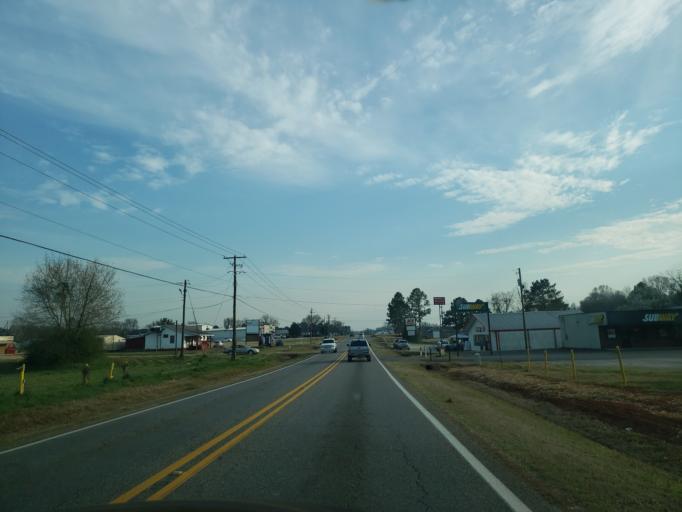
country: US
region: Alabama
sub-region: Hale County
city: Moundville
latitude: 32.9894
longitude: -87.6244
